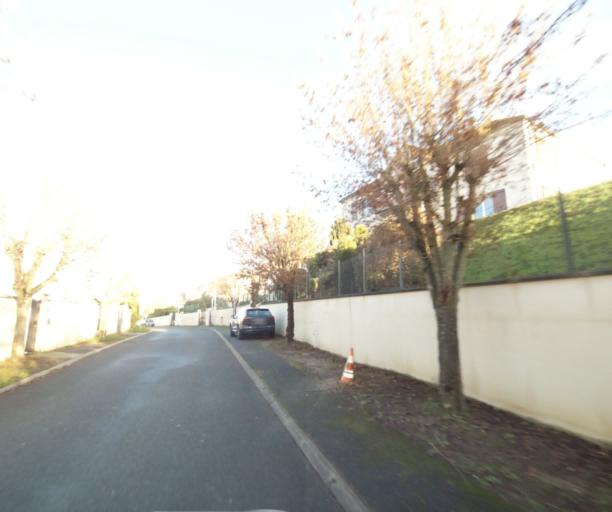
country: FR
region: Ile-de-France
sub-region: Departement des Yvelines
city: Meulan-en-Yvelines
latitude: 49.0131
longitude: 1.9152
